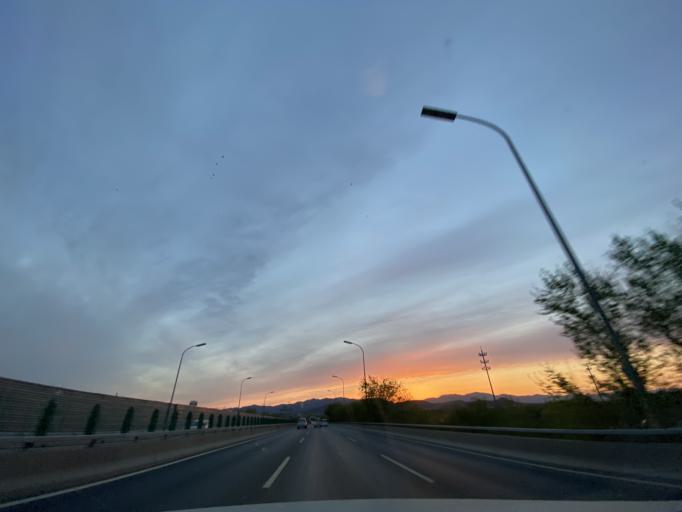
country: CN
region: Beijing
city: Qinghe
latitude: 40.0167
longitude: 116.3082
